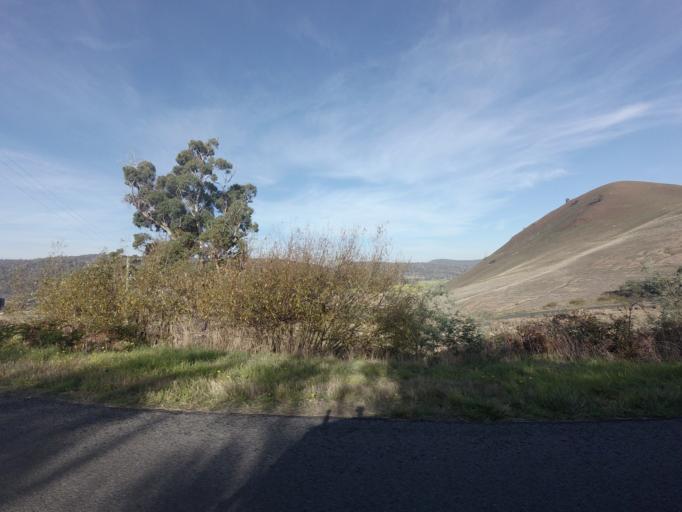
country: AU
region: Tasmania
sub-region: Brighton
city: Bridgewater
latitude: -42.5151
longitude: 147.4064
